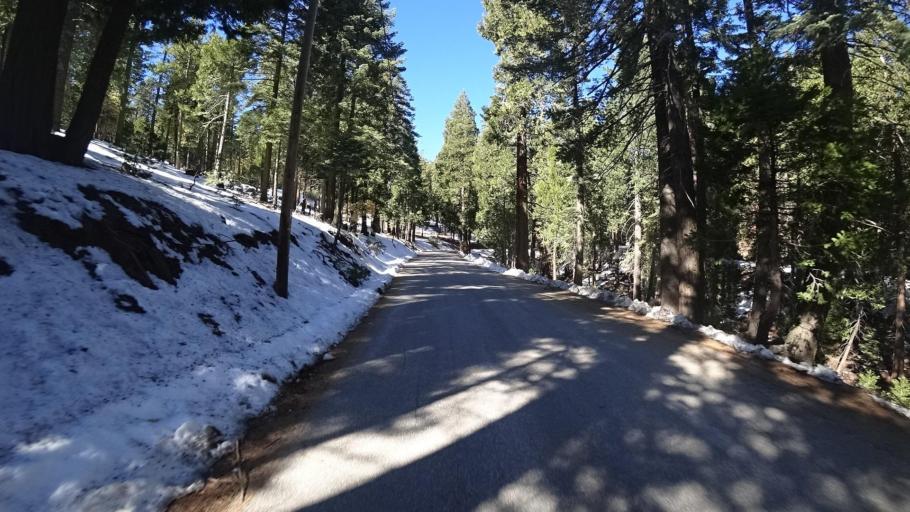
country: US
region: California
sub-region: Kern County
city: Alta Sierra
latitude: 35.7348
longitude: -118.5540
